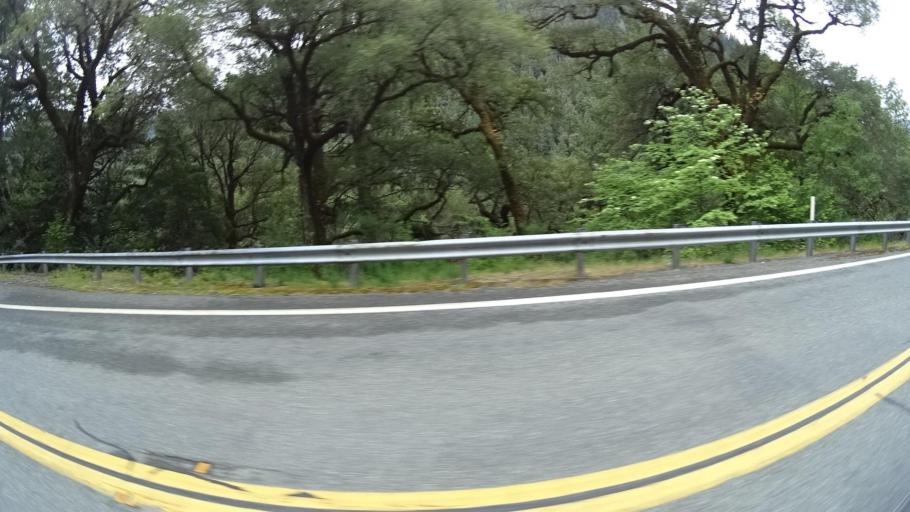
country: US
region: California
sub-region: Humboldt County
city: Willow Creek
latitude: 41.2597
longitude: -123.6090
